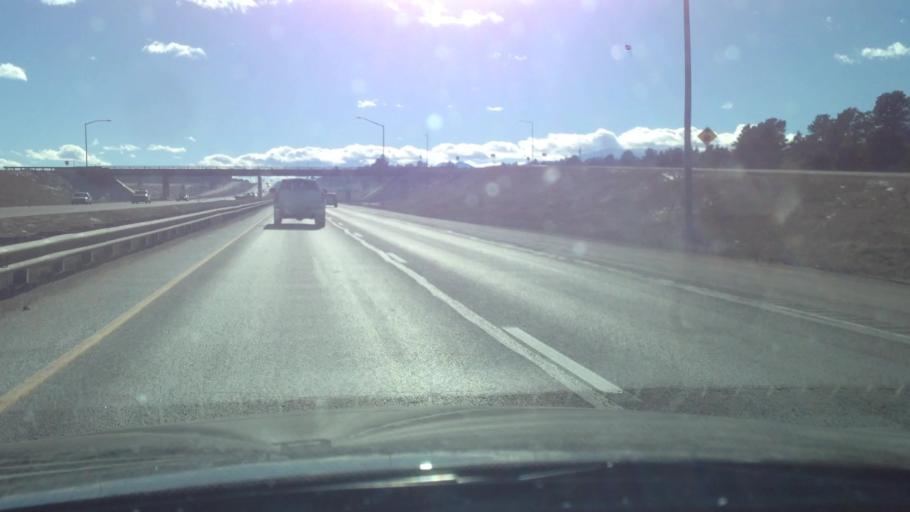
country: US
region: Colorado
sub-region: El Paso County
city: Woodmoor
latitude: 39.1320
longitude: -104.8636
